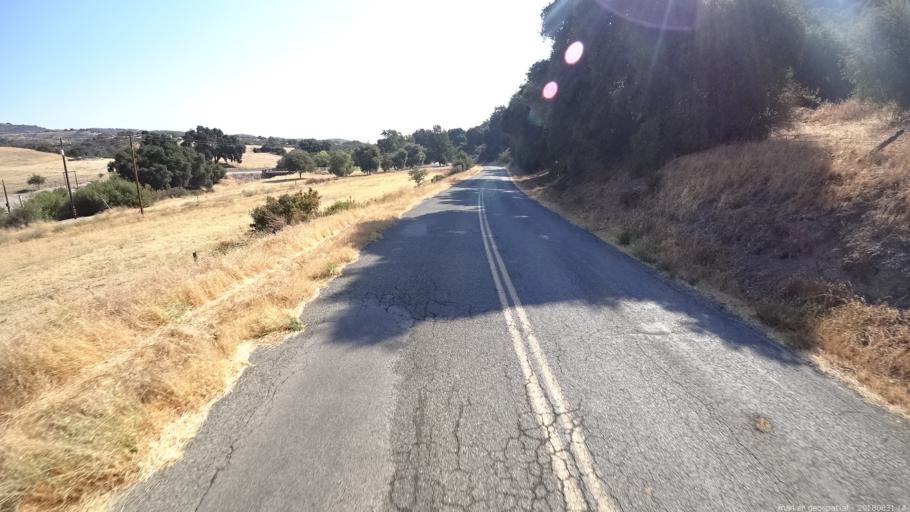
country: US
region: California
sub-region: Monterey County
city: King City
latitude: 36.1502
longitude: -121.1913
